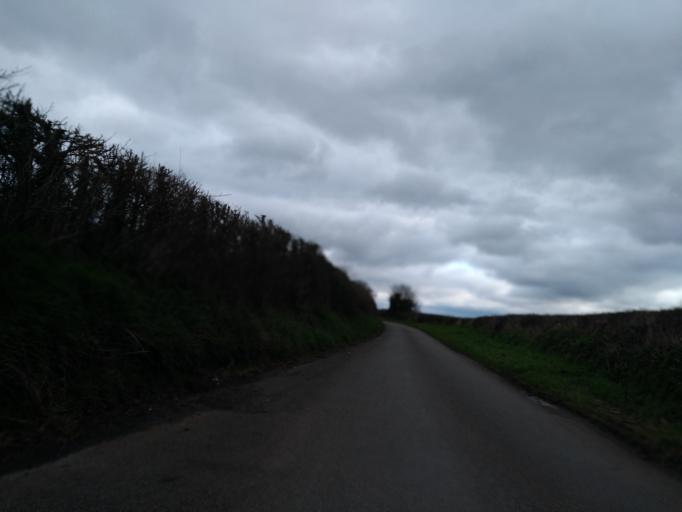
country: GB
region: England
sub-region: Devon
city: Crediton
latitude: 50.7874
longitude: -3.6178
